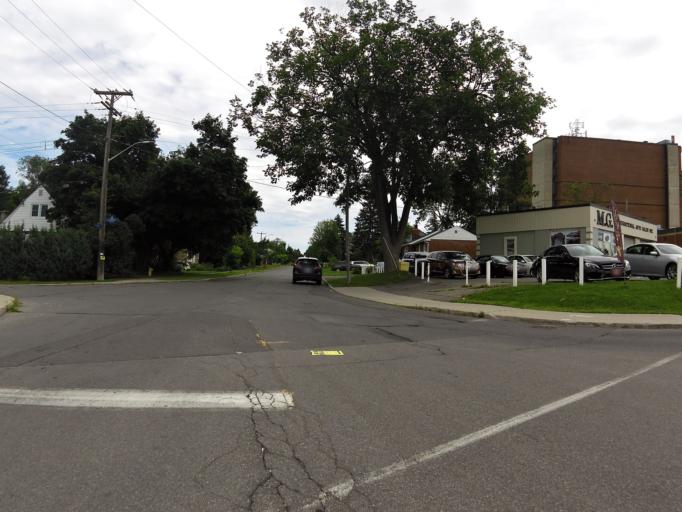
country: CA
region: Ontario
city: Ottawa
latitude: 45.3825
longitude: -75.6706
